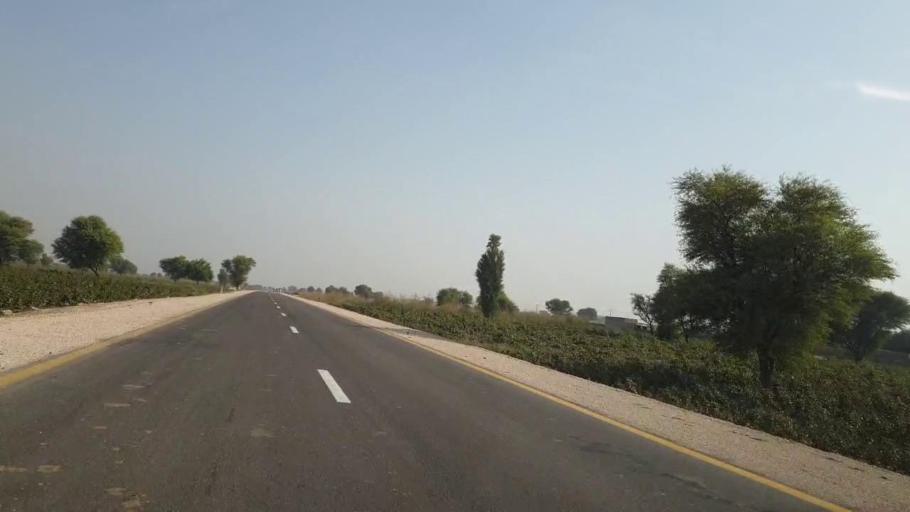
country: PK
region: Sindh
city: Sehwan
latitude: 26.4680
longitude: 67.7951
